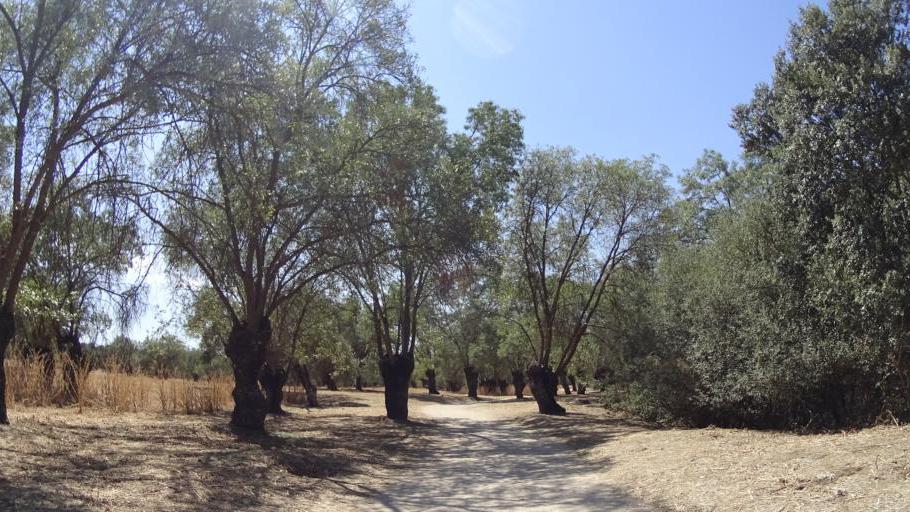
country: ES
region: Madrid
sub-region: Provincia de Madrid
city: Boadilla del Monte
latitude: 40.4117
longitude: -3.8669
